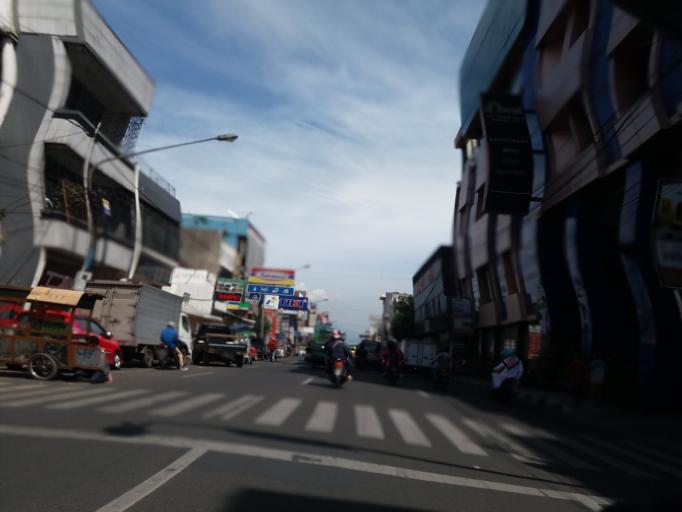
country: ID
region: West Java
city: Bandung
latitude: -6.9296
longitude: 107.6035
